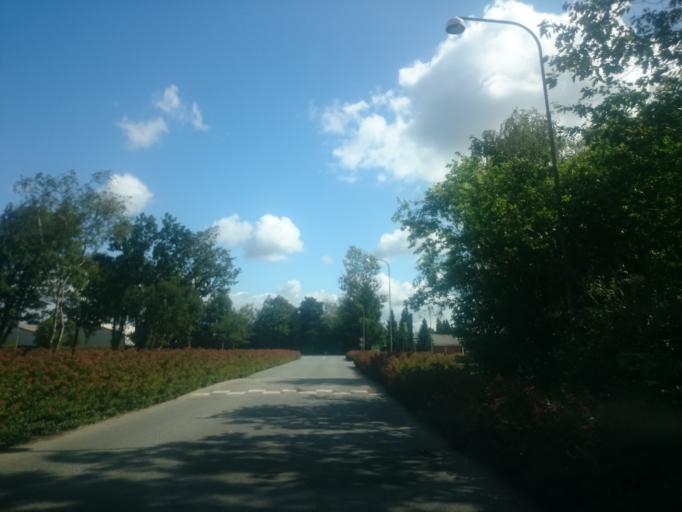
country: DK
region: South Denmark
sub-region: Billund Kommune
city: Billund
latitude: 55.7239
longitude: 9.1197
